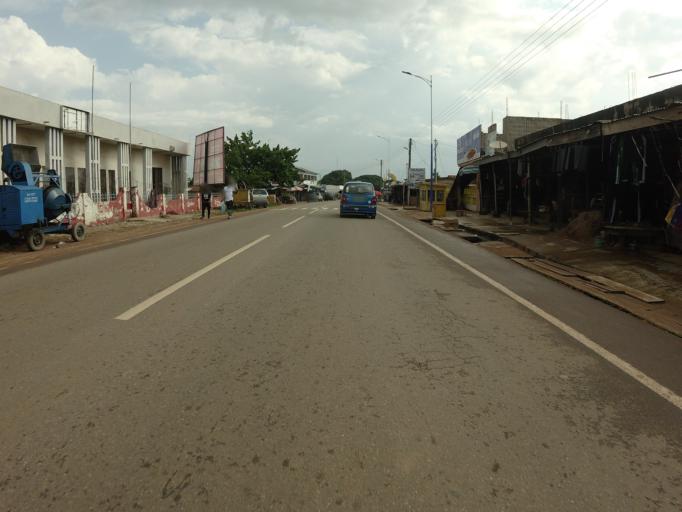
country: GH
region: Volta
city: Hohoe
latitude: 7.1525
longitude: 0.4754
